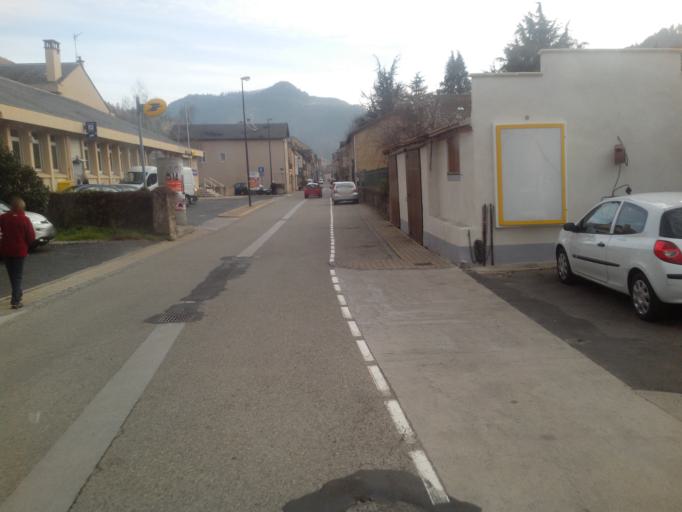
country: FR
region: Languedoc-Roussillon
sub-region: Departement de la Lozere
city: Florac
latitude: 44.3284
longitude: 3.5922
